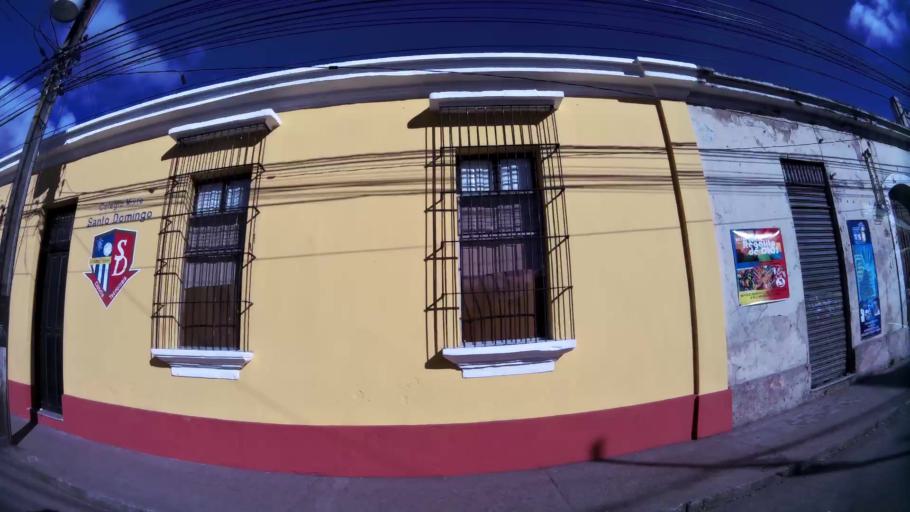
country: GT
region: Guatemala
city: Guatemala City
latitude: 14.6360
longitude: -90.5076
